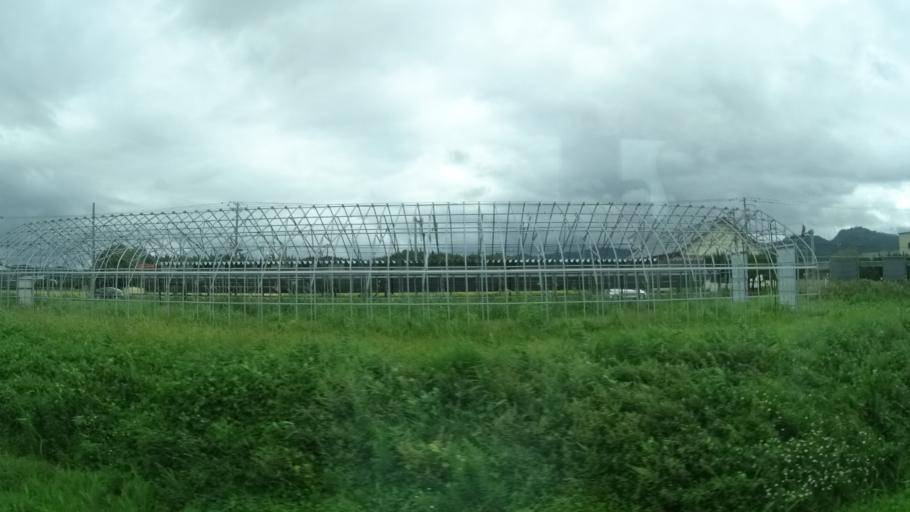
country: JP
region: Niigata
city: Murakami
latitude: 38.1547
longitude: 139.4592
